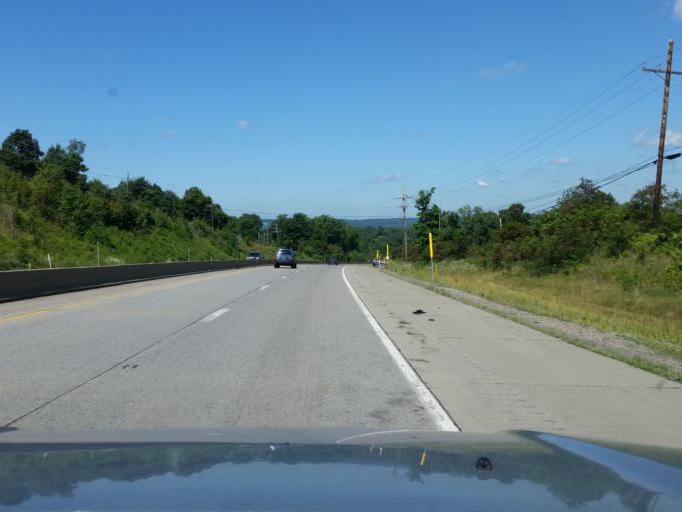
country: US
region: Pennsylvania
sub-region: Cambria County
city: Vinco
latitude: 40.4427
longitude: -78.9641
